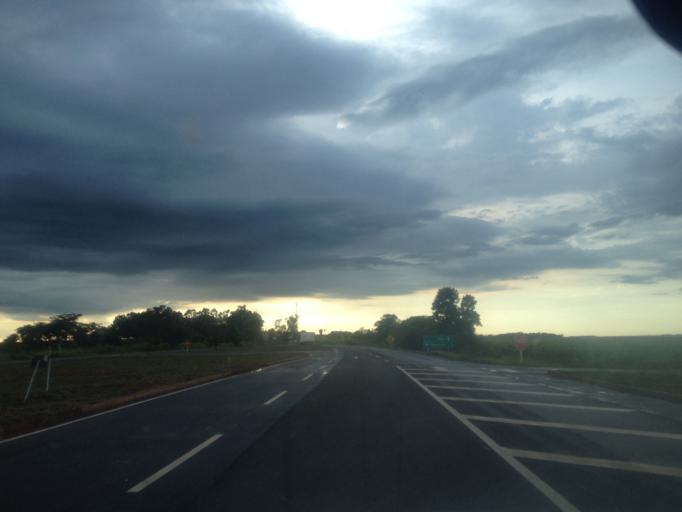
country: BR
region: Goias
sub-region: Jatai
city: Jatai
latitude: -17.8005
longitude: -52.0481
